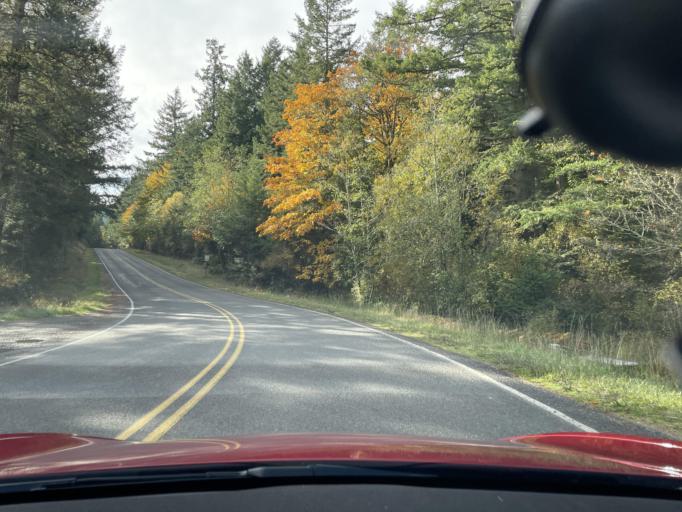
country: US
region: Washington
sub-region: San Juan County
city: Friday Harbor
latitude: 48.5980
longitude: -123.1321
